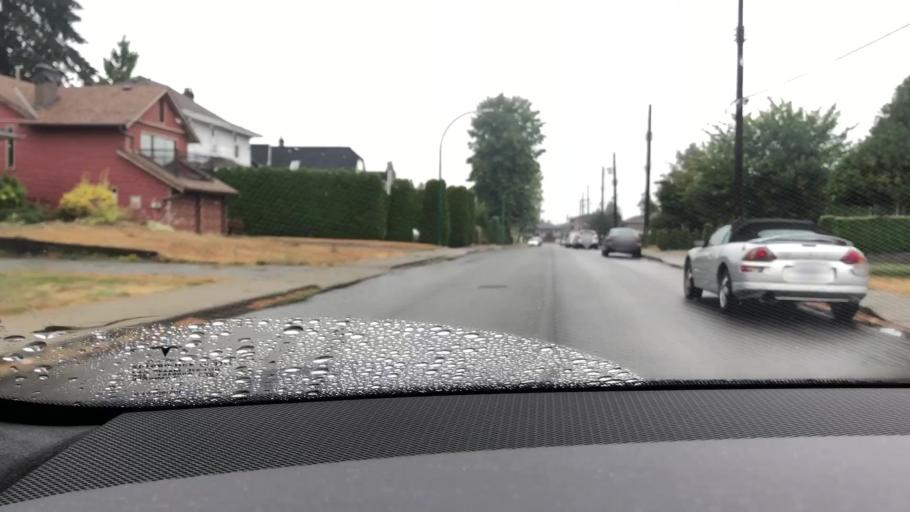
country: CA
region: British Columbia
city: Burnaby
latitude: 49.2228
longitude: -122.9541
